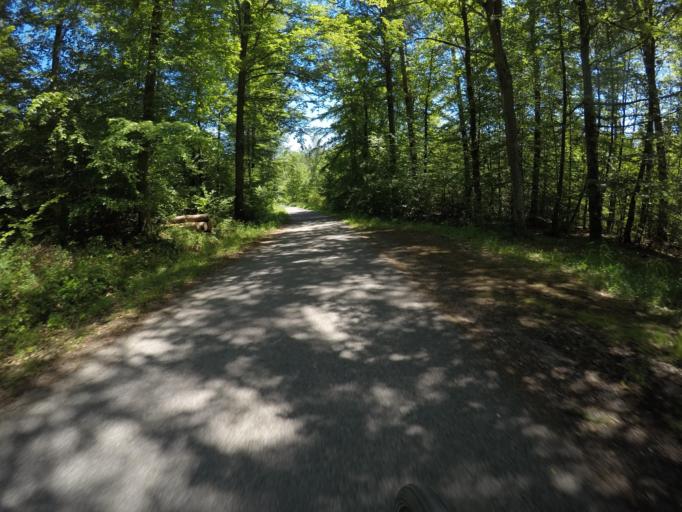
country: DE
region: Baden-Wuerttemberg
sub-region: Regierungsbezirk Stuttgart
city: Gerlingen
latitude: 48.7431
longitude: 9.0670
